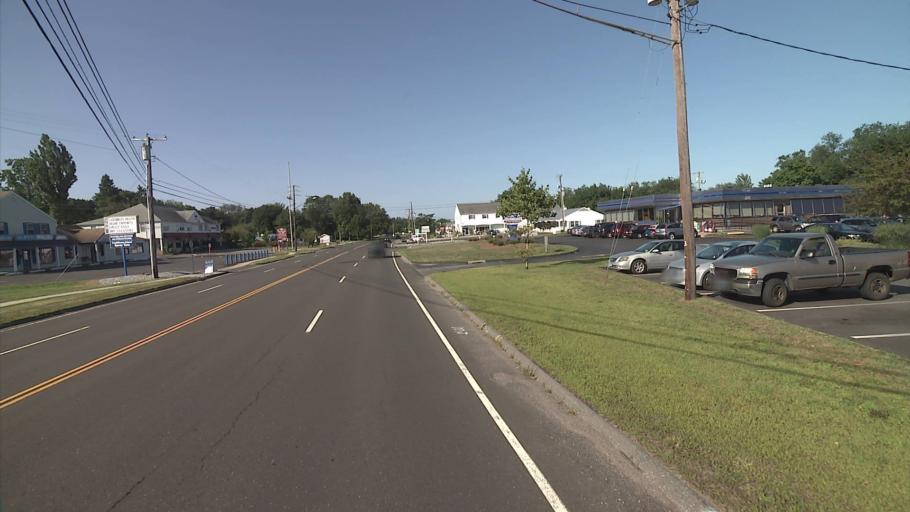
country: US
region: Connecticut
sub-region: Middlesex County
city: Old Saybrook
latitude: 41.2924
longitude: -72.3829
